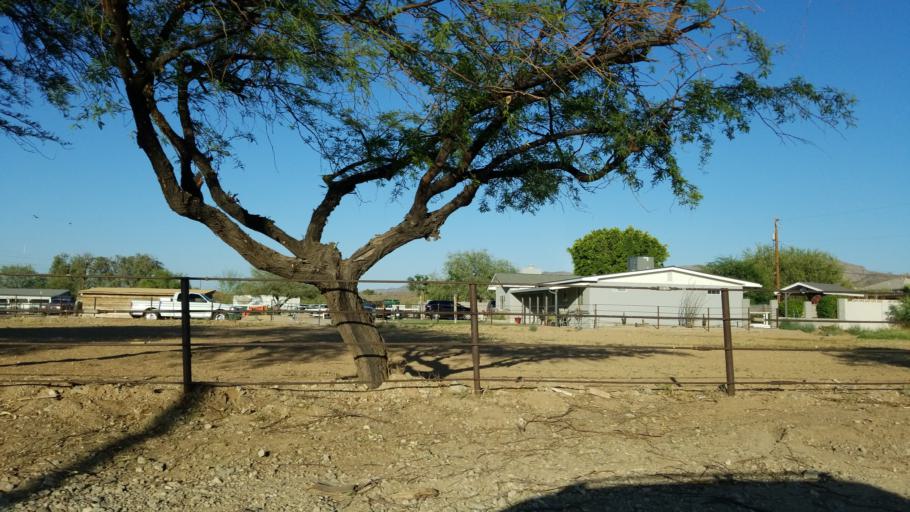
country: US
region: Arizona
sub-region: Maricopa County
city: Laveen
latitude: 33.3620
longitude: -112.1176
